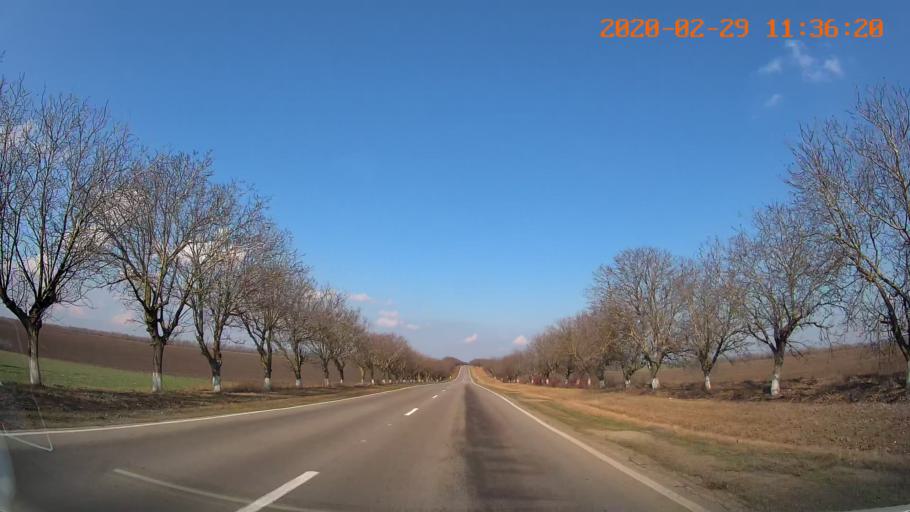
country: MD
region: Rezina
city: Saharna
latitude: 47.5943
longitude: 29.0569
